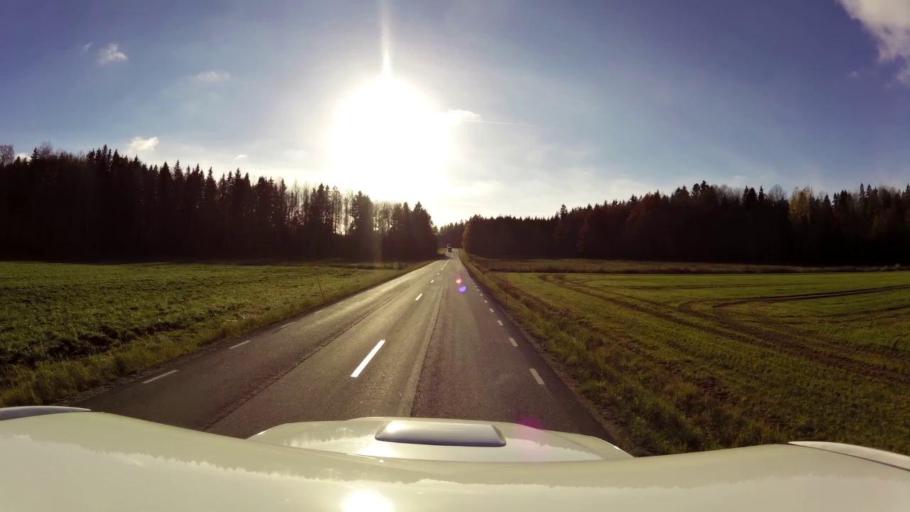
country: SE
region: OEstergoetland
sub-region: Linkopings Kommun
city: Malmslatt
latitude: 58.3248
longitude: 15.5036
